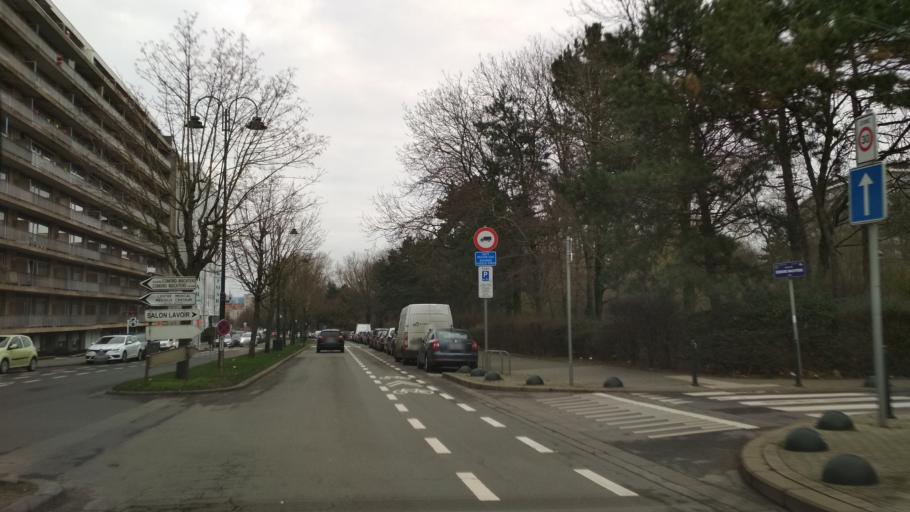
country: BE
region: Brussels Capital
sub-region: Bruxelles-Capitale
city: Brussels
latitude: 50.8516
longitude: 4.3128
